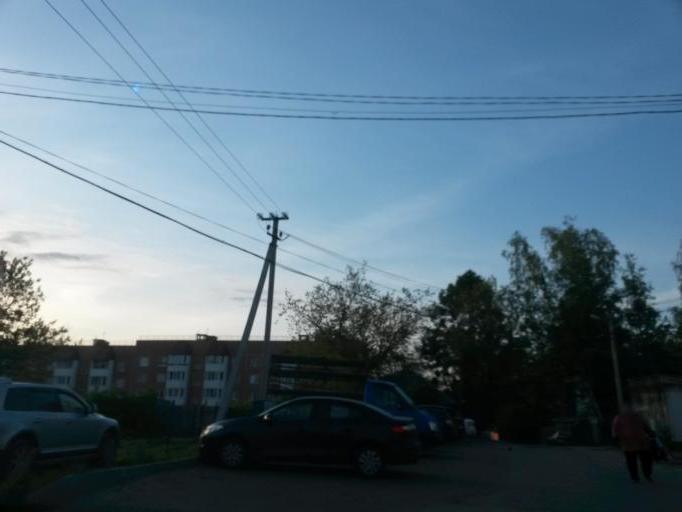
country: RU
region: Moskovskaya
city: Lyubuchany
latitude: 55.2420
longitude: 37.5433
